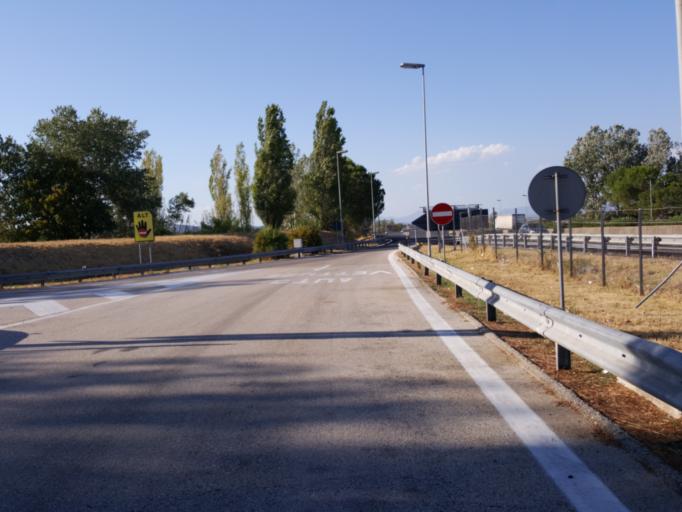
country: IT
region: Latium
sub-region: Citta metropolitana di Roma Capitale
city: Bivio di Capanelle
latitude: 42.1243
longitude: 12.6170
